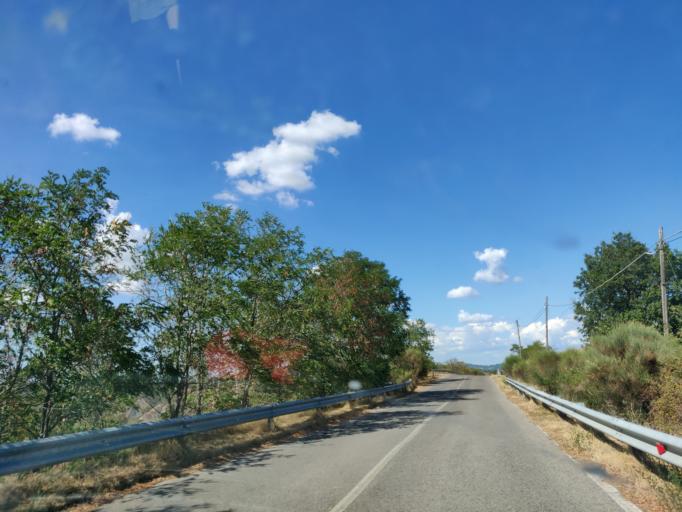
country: IT
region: Tuscany
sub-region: Provincia di Siena
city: Radicofani
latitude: 42.9357
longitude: 11.7322
